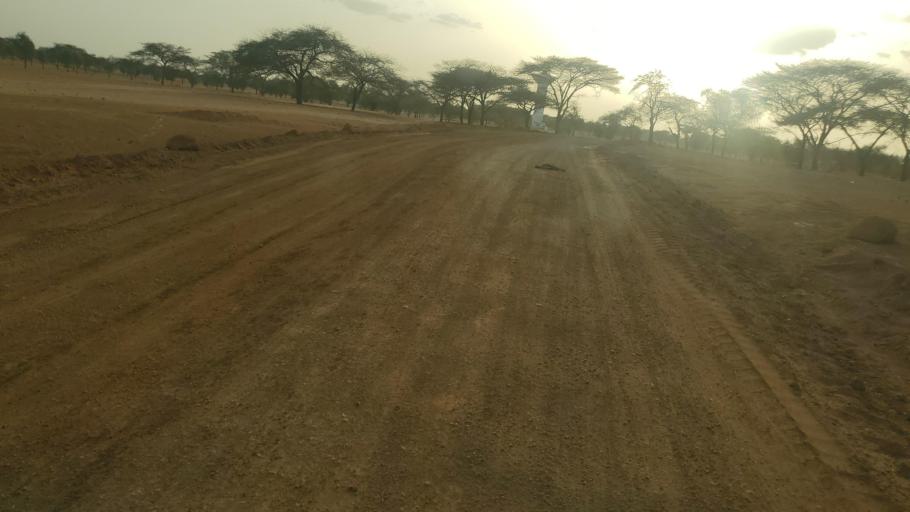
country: SN
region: Louga
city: Dara
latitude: 15.3657
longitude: -15.5623
